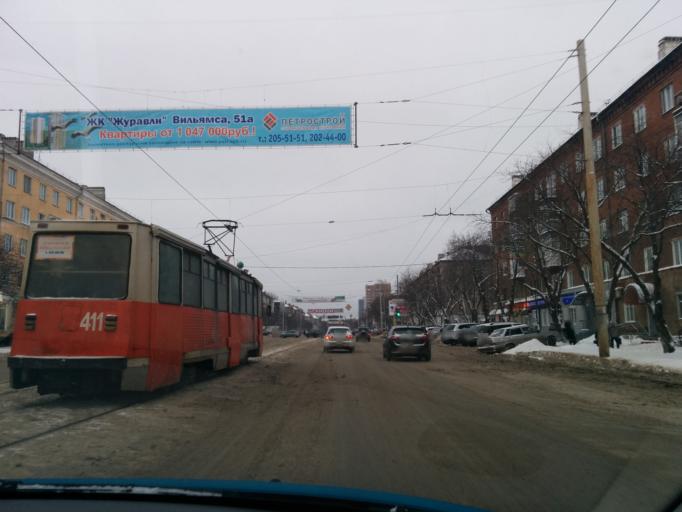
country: RU
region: Perm
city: Perm
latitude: 58.0186
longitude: 56.2778
